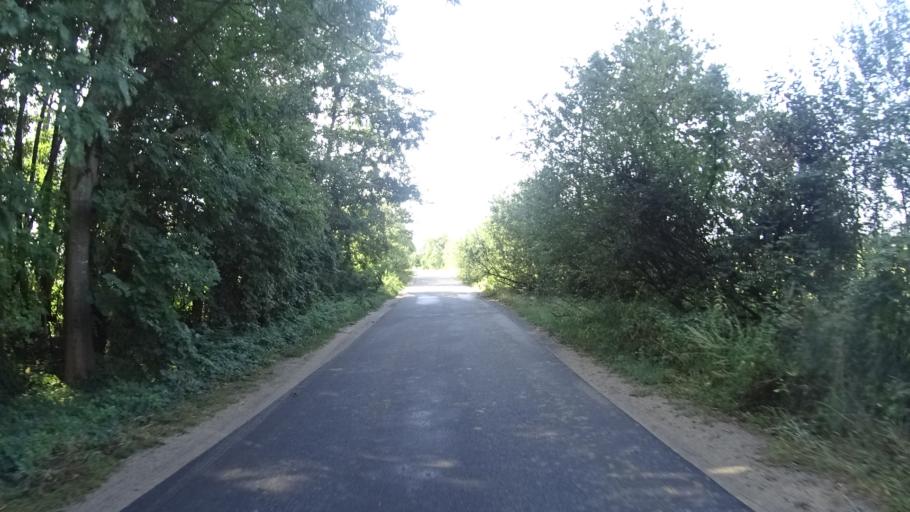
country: DE
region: Brandenburg
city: Straupitz
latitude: 51.8947
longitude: 14.1250
